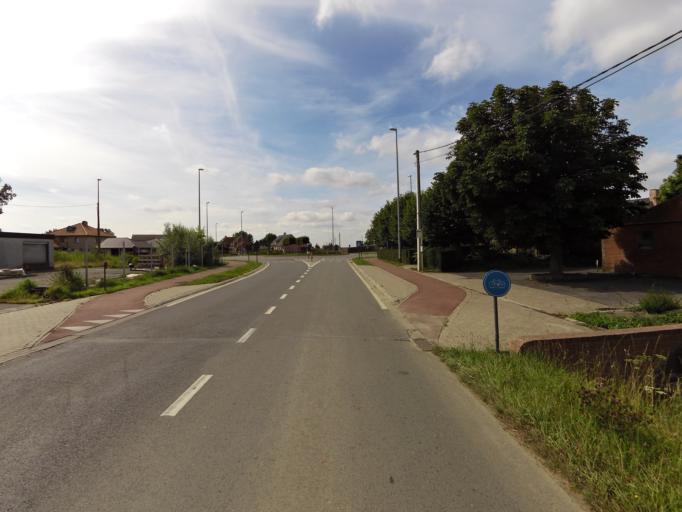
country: BE
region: Flanders
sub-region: Provincie West-Vlaanderen
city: Houthulst
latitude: 50.9398
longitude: 2.9395
